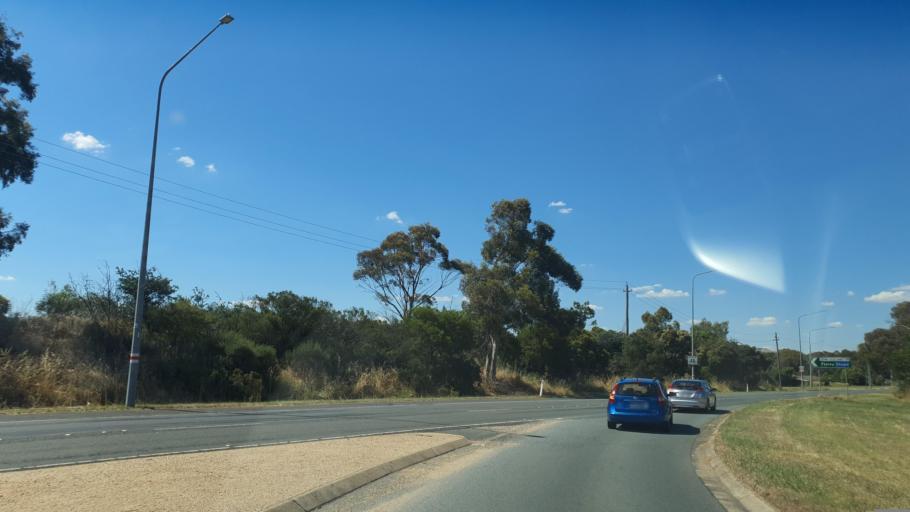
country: AU
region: Australian Capital Territory
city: Macquarie
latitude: -35.2277
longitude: 149.0598
